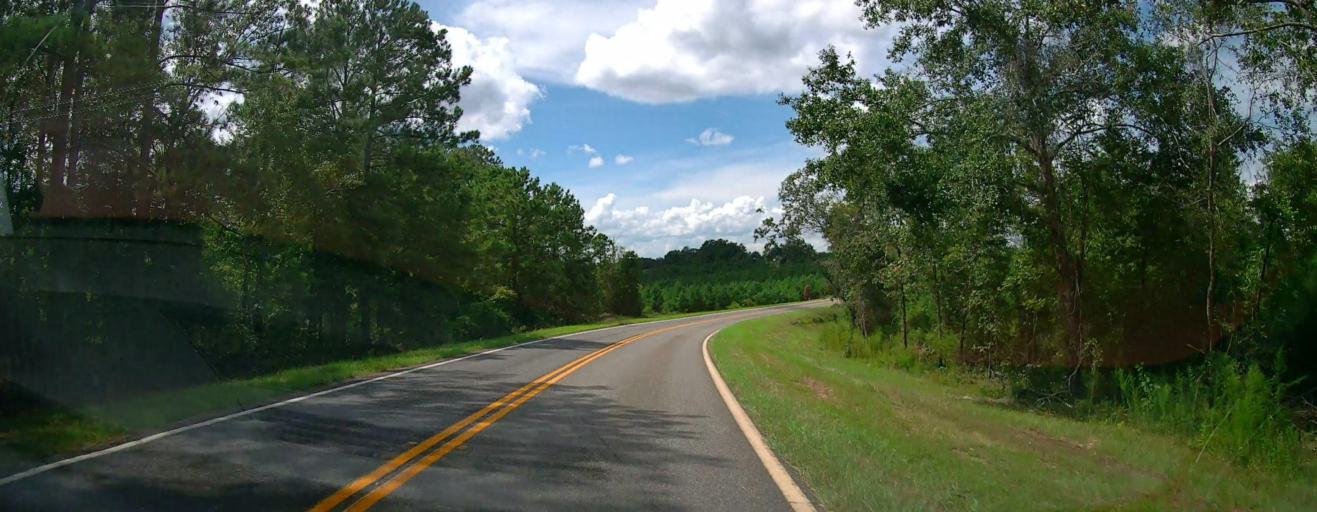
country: US
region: Georgia
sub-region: Taylor County
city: Butler
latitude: 32.4344
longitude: -84.1866
